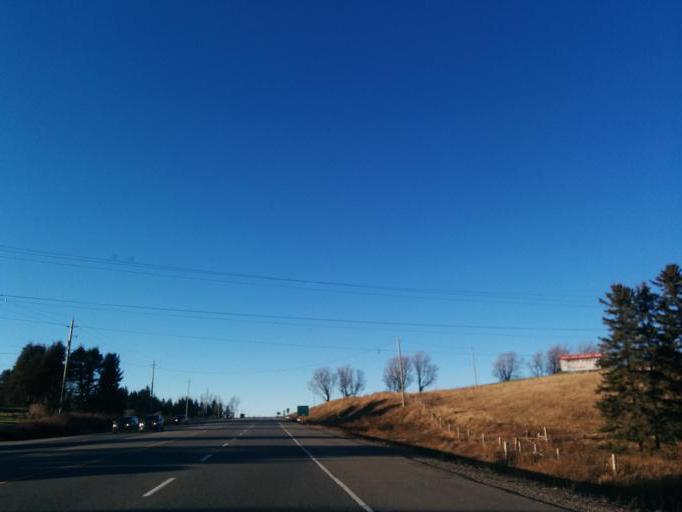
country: CA
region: Ontario
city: Orangeville
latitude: 43.9112
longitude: -80.0653
